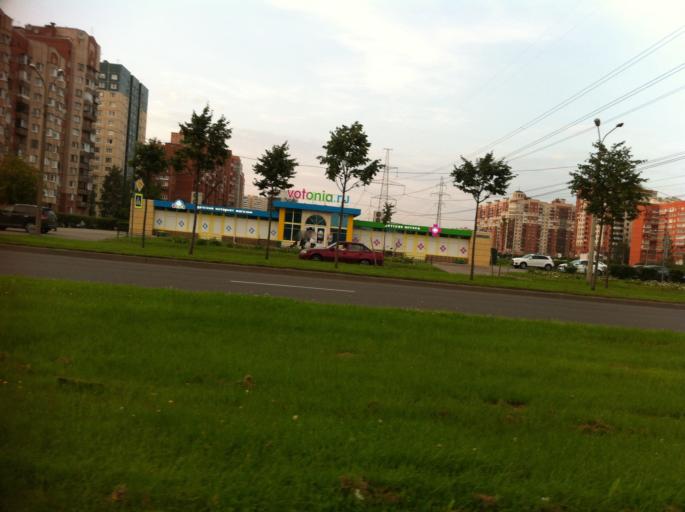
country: RU
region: St.-Petersburg
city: Uritsk
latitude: 59.8527
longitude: 30.1968
